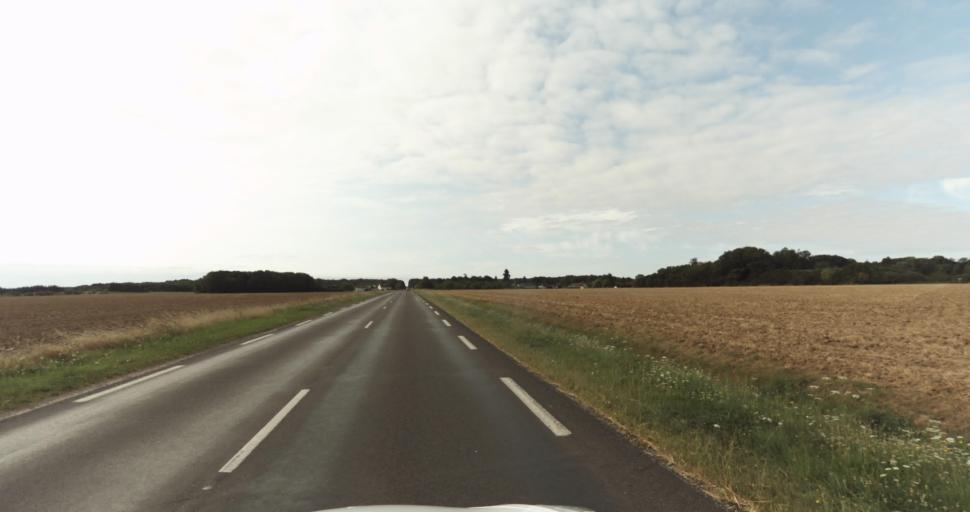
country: FR
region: Haute-Normandie
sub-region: Departement de l'Eure
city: La Madeleine-de-Nonancourt
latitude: 48.8281
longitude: 1.1848
